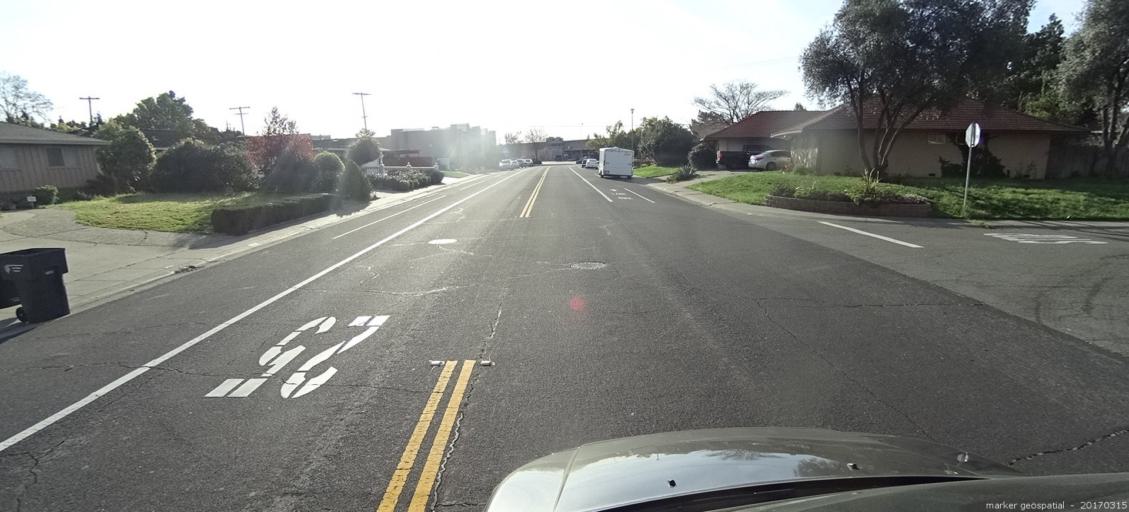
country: US
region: California
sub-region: Sacramento County
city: Parkway
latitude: 38.4979
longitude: -121.5121
